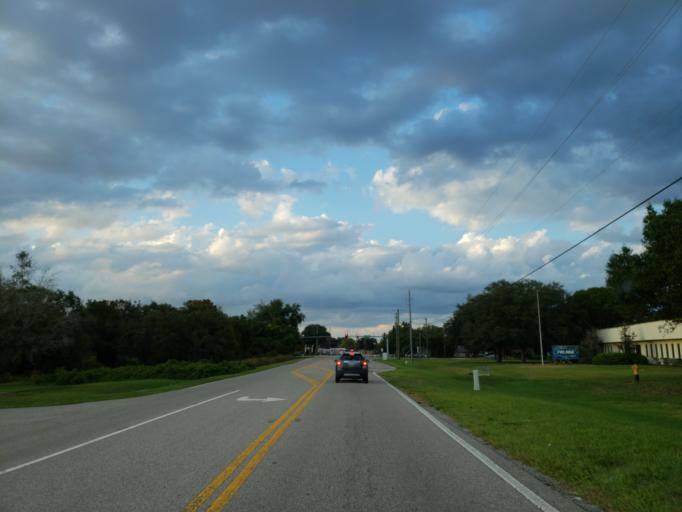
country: US
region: Florida
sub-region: Pasco County
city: Odessa
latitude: 28.1861
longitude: -82.5919
